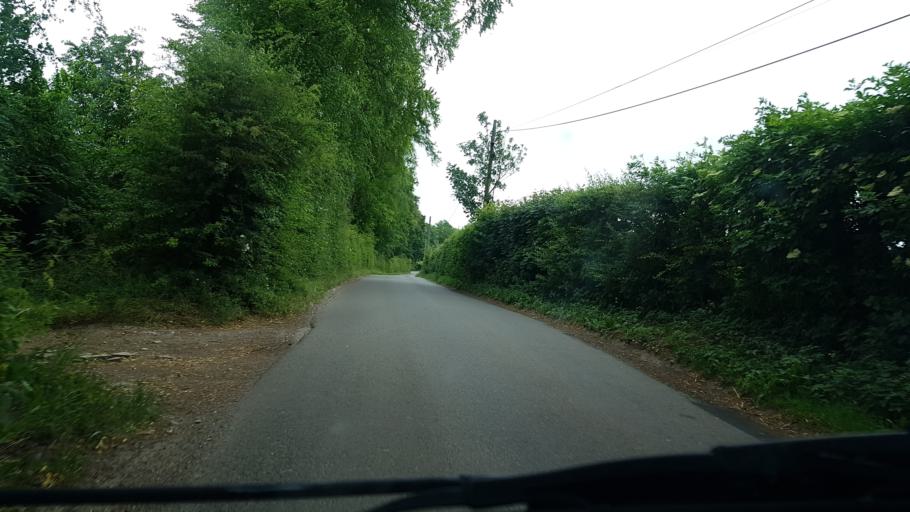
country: GB
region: England
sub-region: Surrey
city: Great Bookham
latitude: 51.2657
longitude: -0.3683
